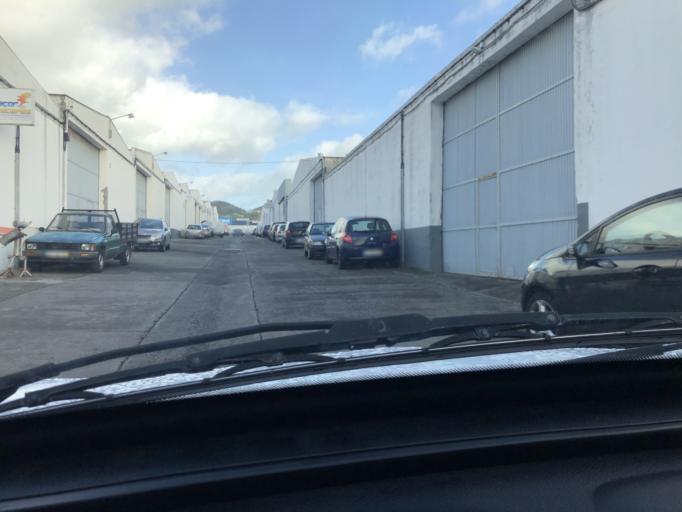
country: PT
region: Azores
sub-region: Ponta Delgada
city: Rosto de Cao
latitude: 37.7495
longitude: -25.6564
